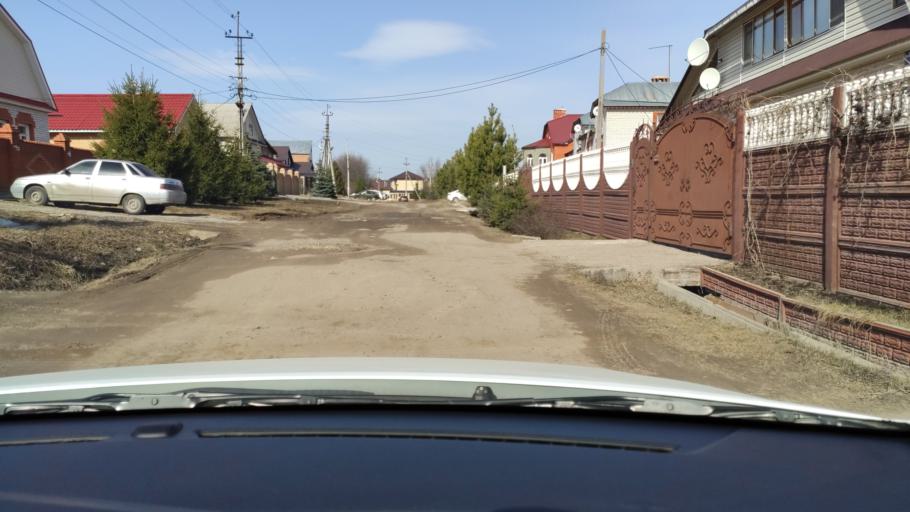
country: RU
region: Tatarstan
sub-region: Gorod Kazan'
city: Kazan
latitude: 55.7856
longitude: 49.2477
